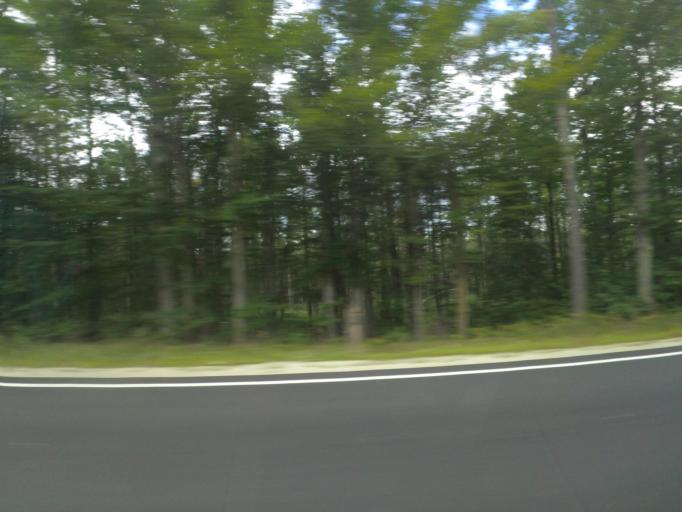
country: US
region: New Hampshire
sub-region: Rockingham County
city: Northwood
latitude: 43.2015
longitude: -71.1093
